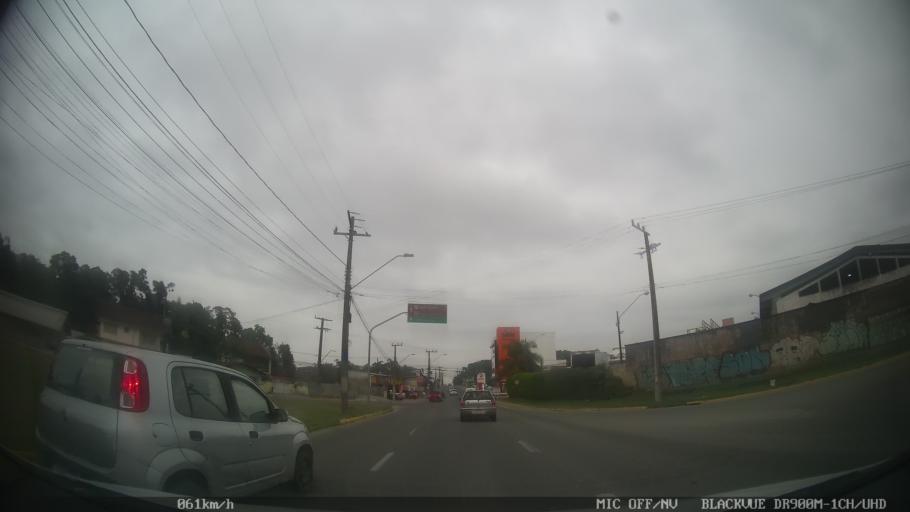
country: BR
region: Santa Catarina
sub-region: Joinville
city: Joinville
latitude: -26.3399
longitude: -48.8414
